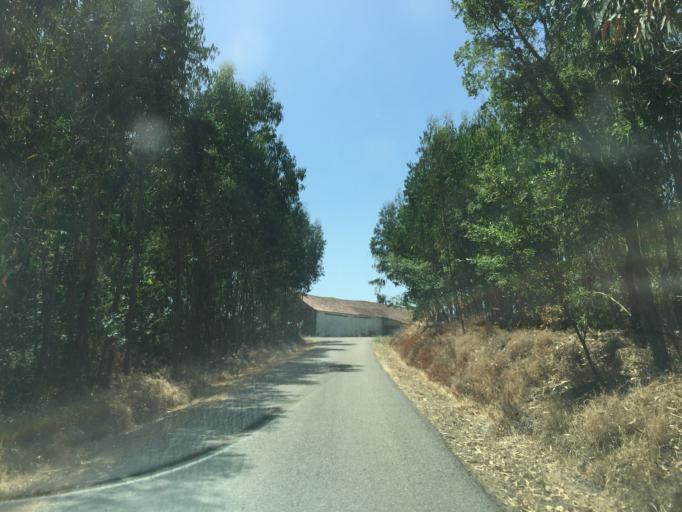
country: PT
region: Santarem
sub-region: Ferreira do Zezere
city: Ferreira do Zezere
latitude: 39.6423
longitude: -8.2971
